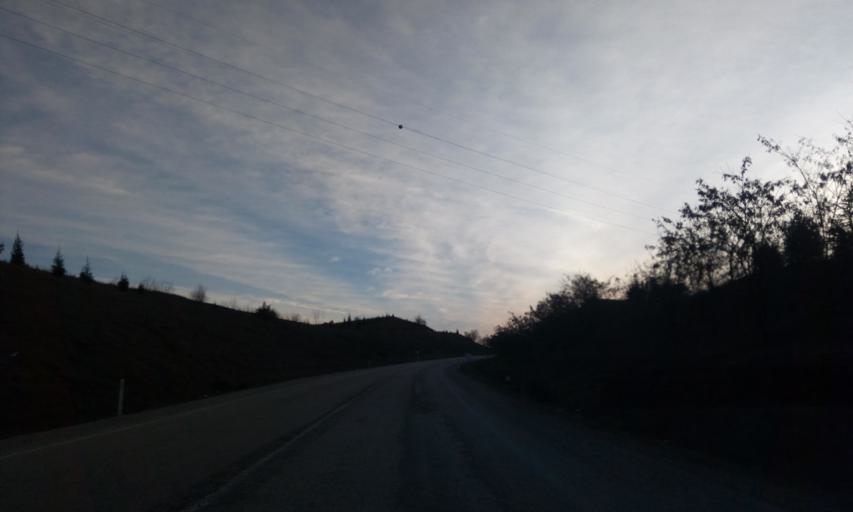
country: TR
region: Bilecik
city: Kuplu
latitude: 40.1100
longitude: 30.0871
